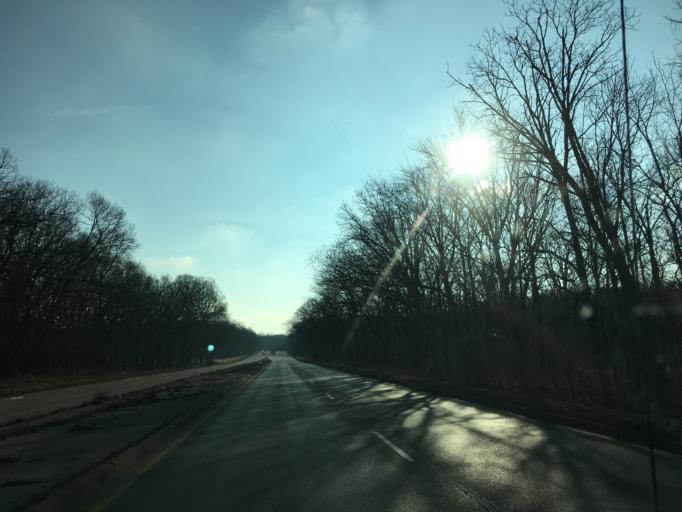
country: US
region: Illinois
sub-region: Cook County
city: Elk Grove Village
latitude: 42.0303
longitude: -88.0036
